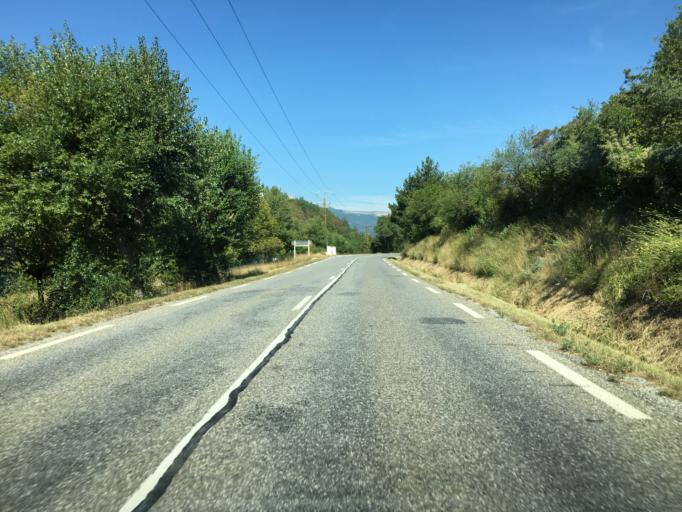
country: FR
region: Provence-Alpes-Cote d'Azur
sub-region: Departement des Hautes-Alpes
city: Laragne-Monteglin
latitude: 44.3369
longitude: 5.7810
